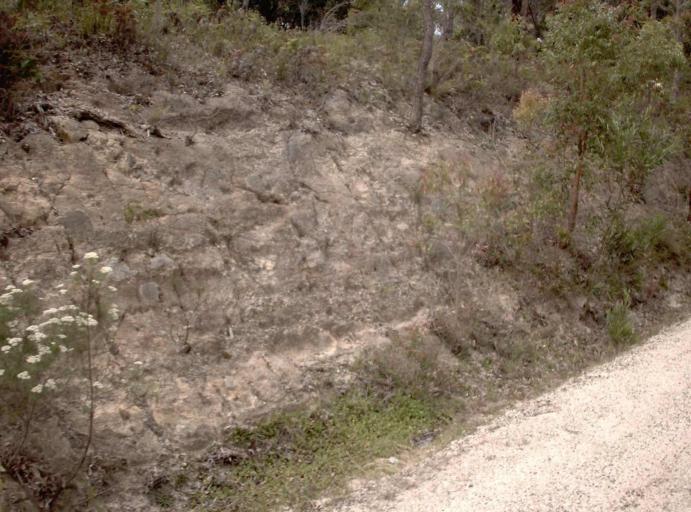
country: AU
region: New South Wales
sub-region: Bega Valley
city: Eden
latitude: -37.4041
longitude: 149.6661
